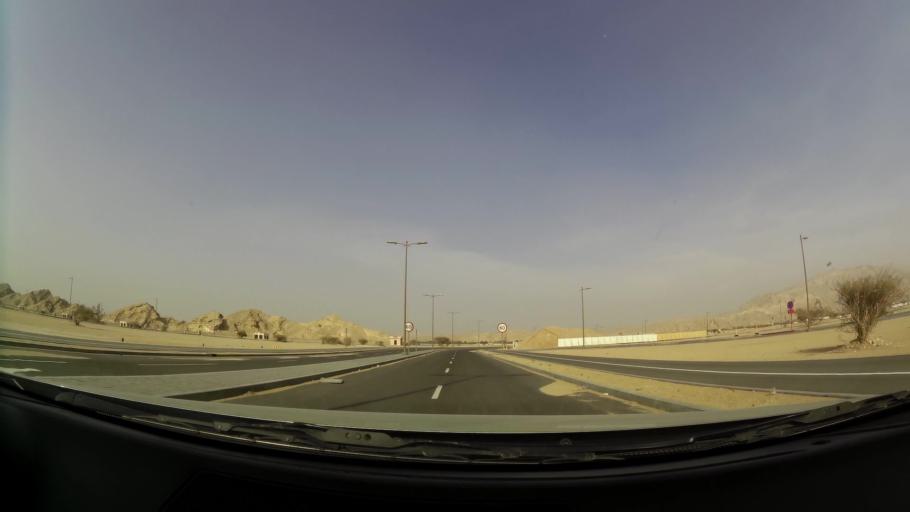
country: AE
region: Abu Dhabi
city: Al Ain
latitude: 24.1237
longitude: 55.7230
